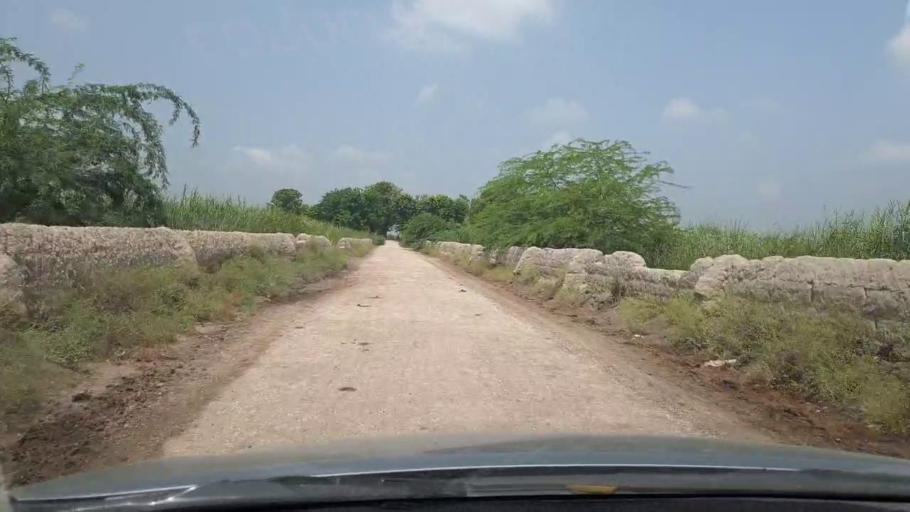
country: PK
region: Sindh
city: Khairpur
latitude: 27.4804
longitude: 68.7109
